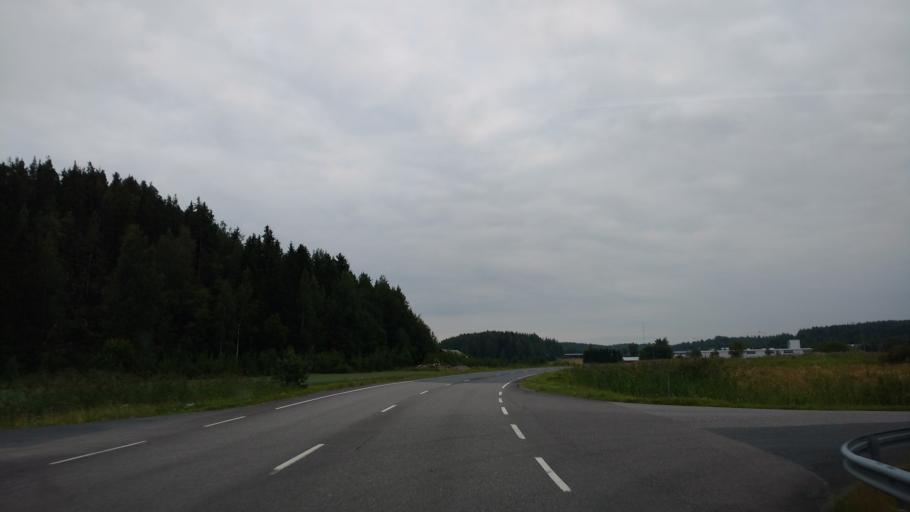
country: FI
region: Varsinais-Suomi
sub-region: Salo
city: Halikko
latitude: 60.3912
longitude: 23.0549
